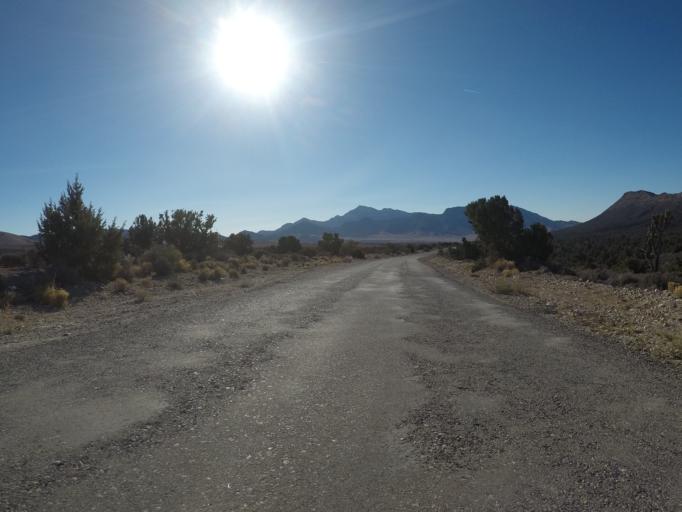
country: US
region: Nevada
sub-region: Clark County
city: Summerlin South
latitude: 36.0722
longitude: -115.5626
